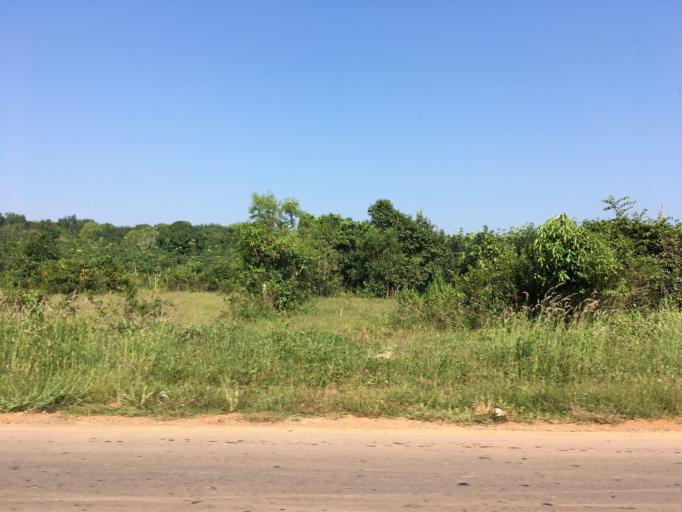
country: MM
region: Mon
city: Martaban
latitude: 16.6953
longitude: 97.7492
